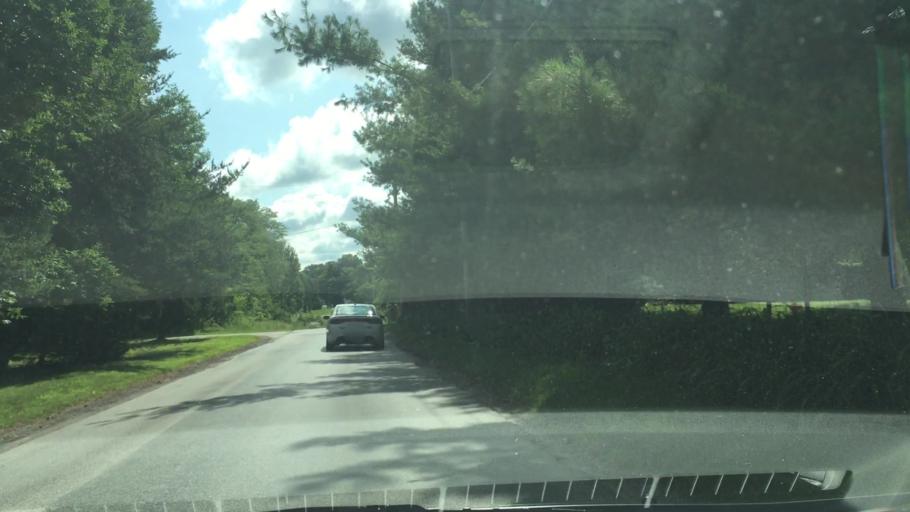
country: US
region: Iowa
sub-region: Johnson County
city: Iowa City
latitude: 41.6894
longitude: -91.5291
